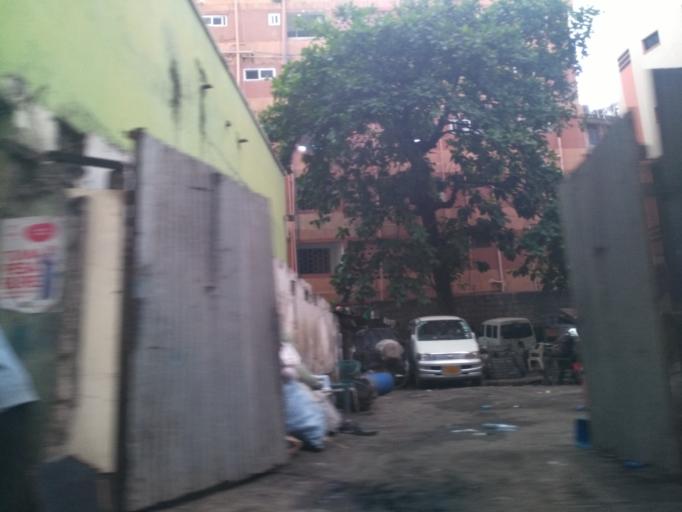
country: TZ
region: Dar es Salaam
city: Dar es Salaam
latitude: -6.8178
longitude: 39.2813
